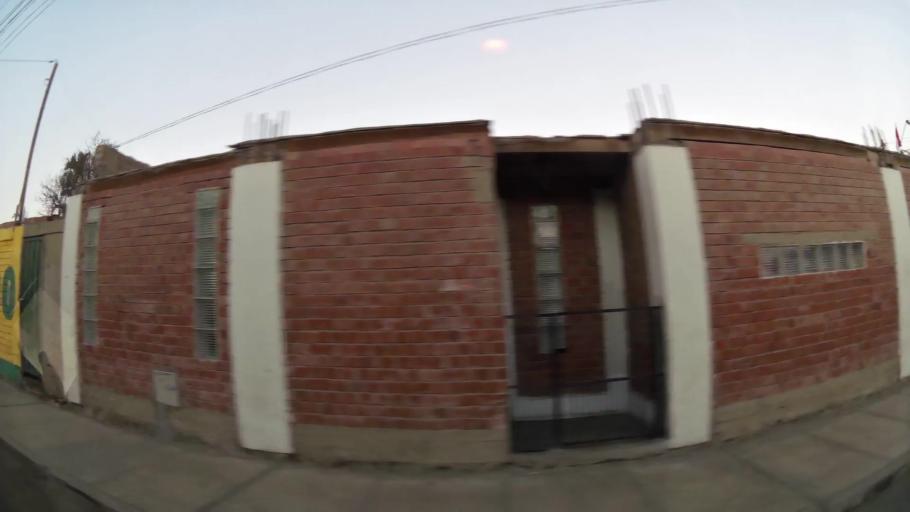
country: PE
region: Ica
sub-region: Provincia de Pisco
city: Pisco
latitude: -13.7105
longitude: -76.1989
